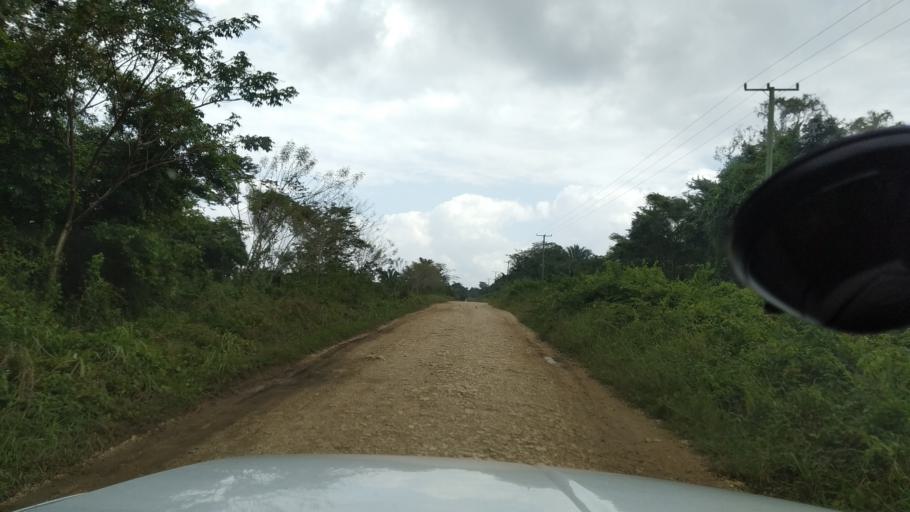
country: BZ
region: Toledo
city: Punta Gorda
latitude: 16.2173
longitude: -89.0037
